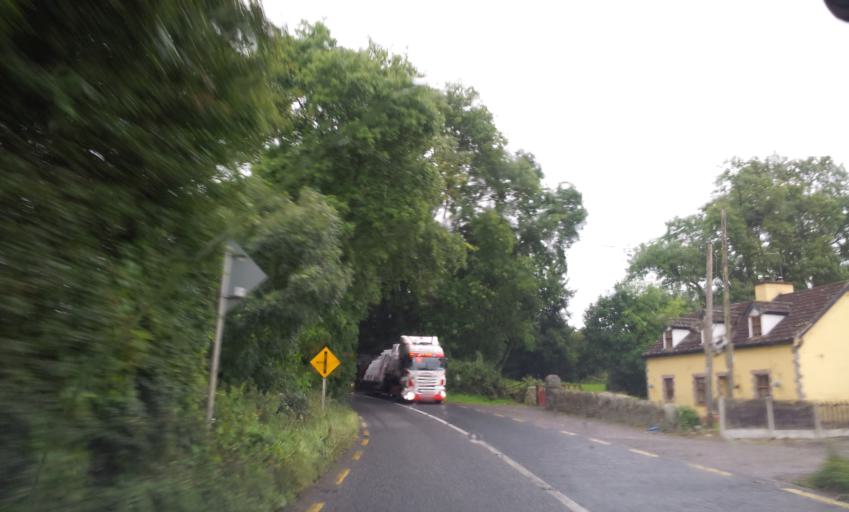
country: IE
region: Munster
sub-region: County Cork
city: Mallow
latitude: 52.1752
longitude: -8.5666
